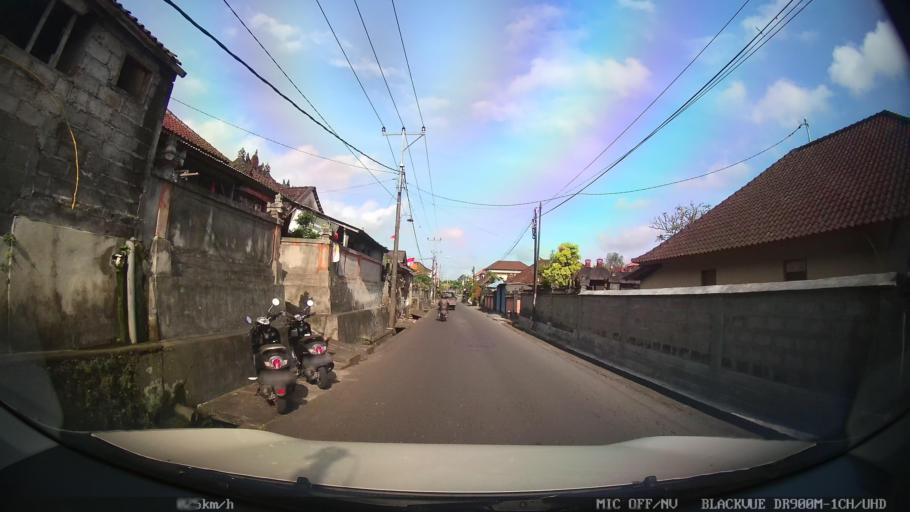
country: ID
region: Bali
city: Banjar Pekenjelodan
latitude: -8.5698
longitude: 115.1840
